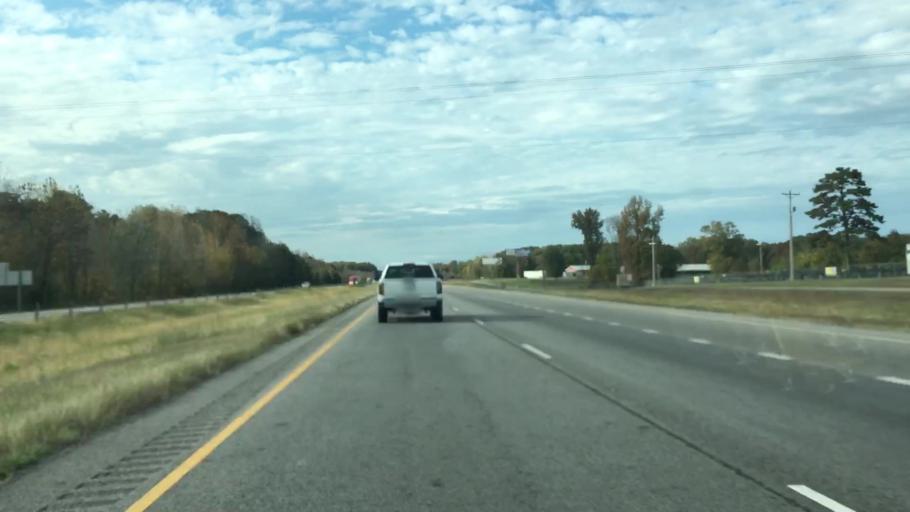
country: US
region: Arkansas
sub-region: Pope County
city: Atkins
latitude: 35.2221
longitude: -92.8336
